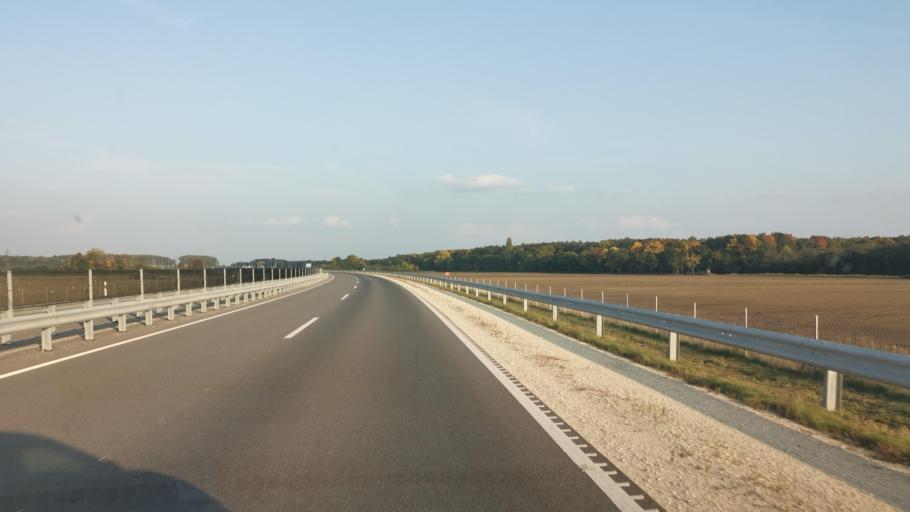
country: HU
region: Gyor-Moson-Sopron
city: Mihalyi
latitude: 47.5614
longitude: 17.0747
